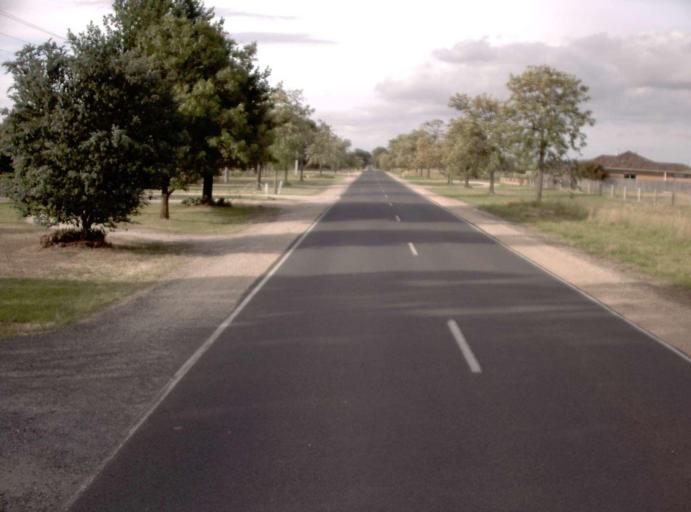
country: AU
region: Victoria
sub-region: Wellington
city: Sale
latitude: -37.9481
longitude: 146.9885
